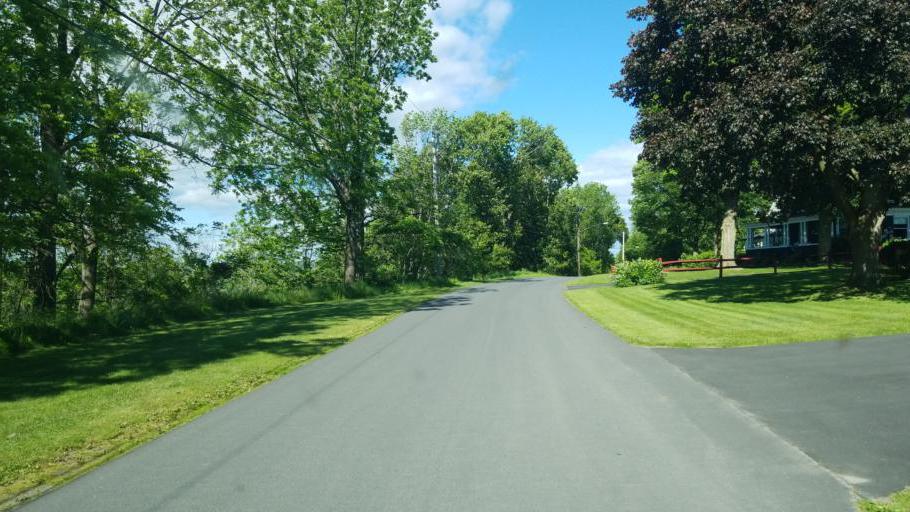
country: US
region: New York
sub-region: Montgomery County
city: Fort Plain
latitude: 42.9283
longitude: -74.6262
